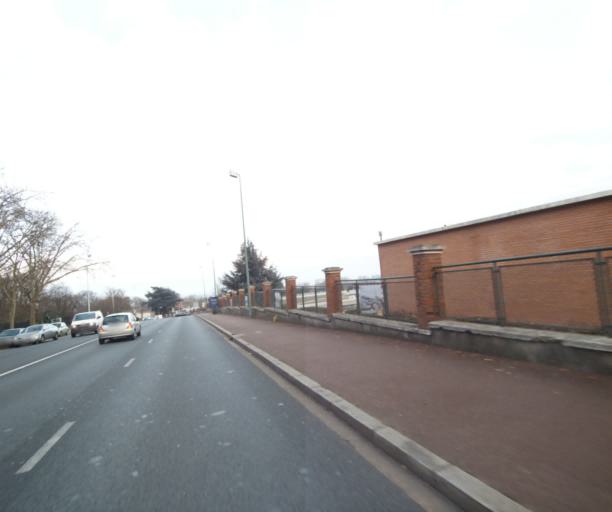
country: FR
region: Ile-de-France
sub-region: Departement des Hauts-de-Seine
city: Suresnes
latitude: 48.8768
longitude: 2.2171
